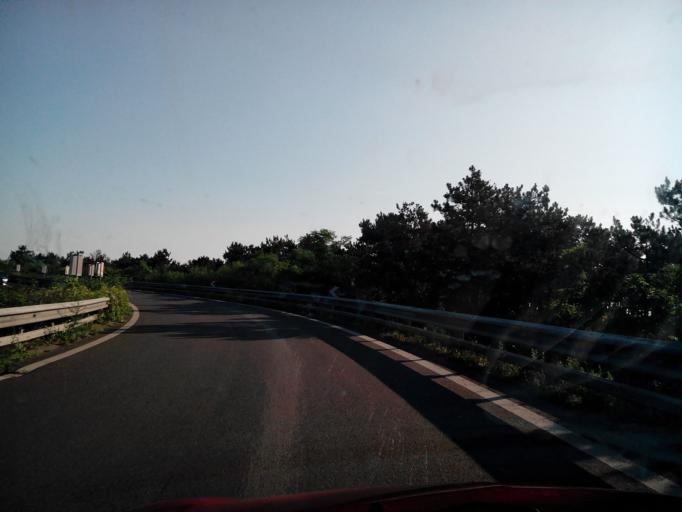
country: AT
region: Lower Austria
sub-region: Politischer Bezirk Baden
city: Traiskirchen
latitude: 47.9847
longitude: 16.2787
